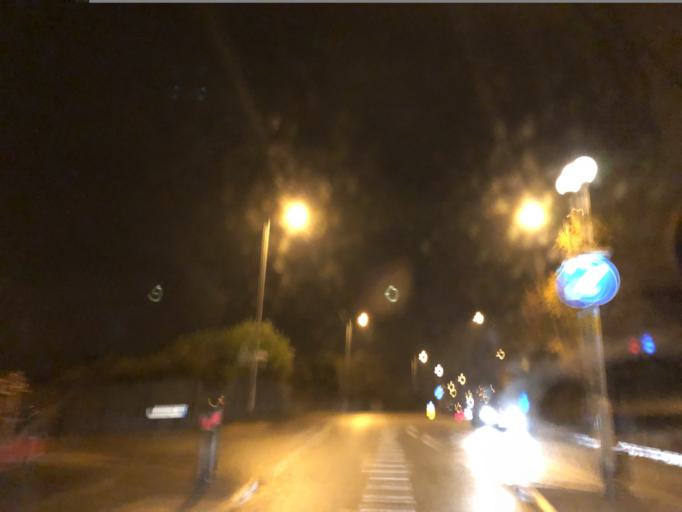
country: GB
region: England
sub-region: Borough of Oldham
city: Shaw
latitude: 53.5564
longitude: -2.0822
